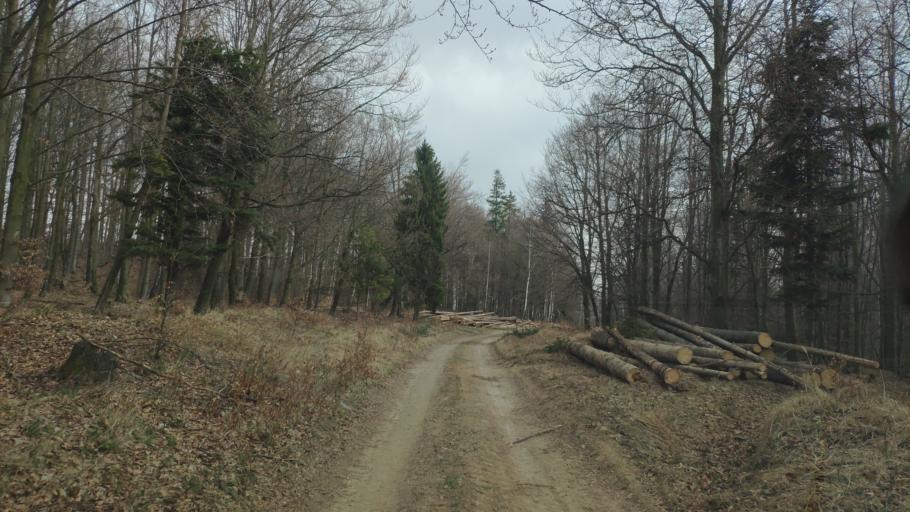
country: SK
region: Kosicky
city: Moldava nad Bodvou
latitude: 48.7430
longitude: 21.0440
